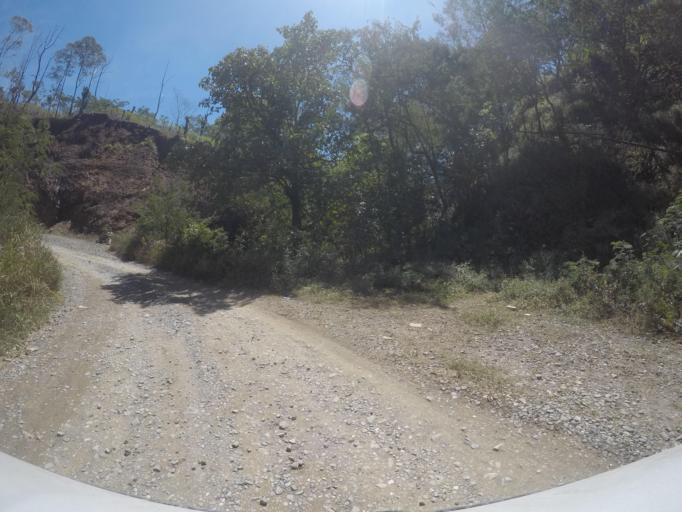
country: TL
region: Ermera
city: Gleno
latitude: -8.7870
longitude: 125.3794
